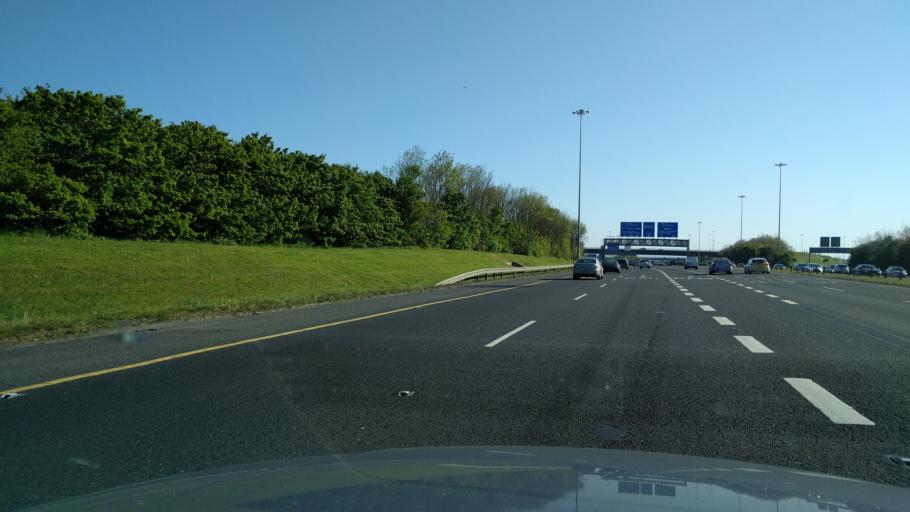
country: IE
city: Bonnybrook
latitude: 53.4168
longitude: -6.2228
